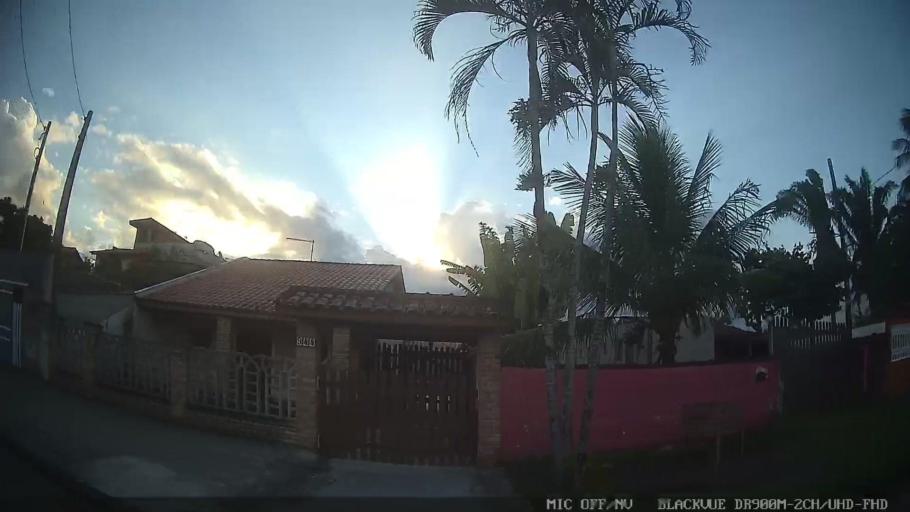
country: BR
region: Sao Paulo
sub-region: Caraguatatuba
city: Caraguatatuba
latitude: -23.6854
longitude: -45.4357
